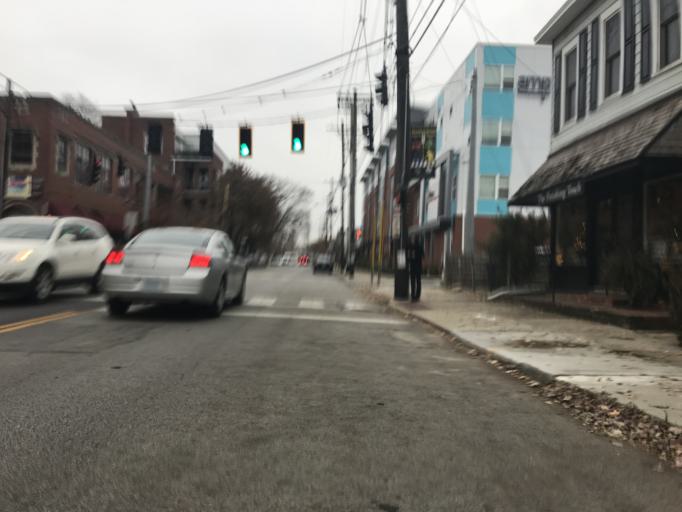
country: US
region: Indiana
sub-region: Clark County
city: Jeffersonville
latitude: 38.2547
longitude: -85.7105
